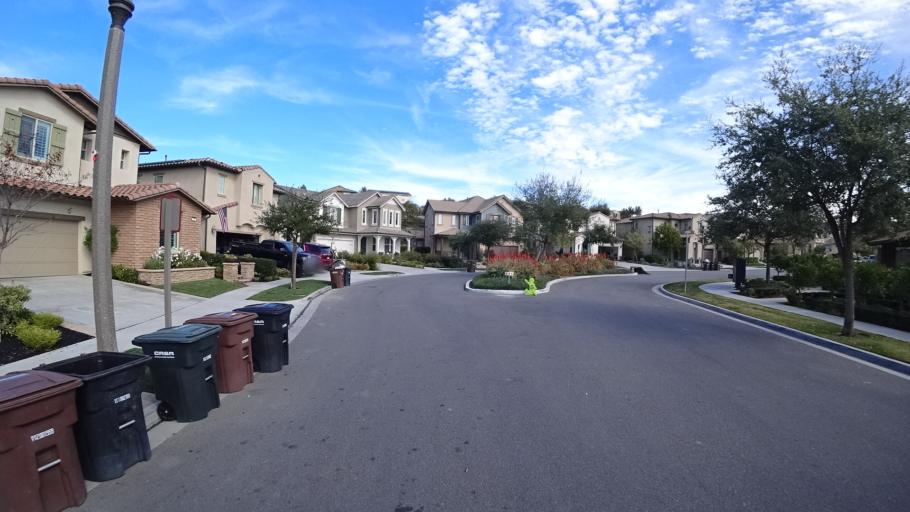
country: US
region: California
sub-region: Orange County
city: Ladera Ranch
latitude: 33.5291
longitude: -117.6234
